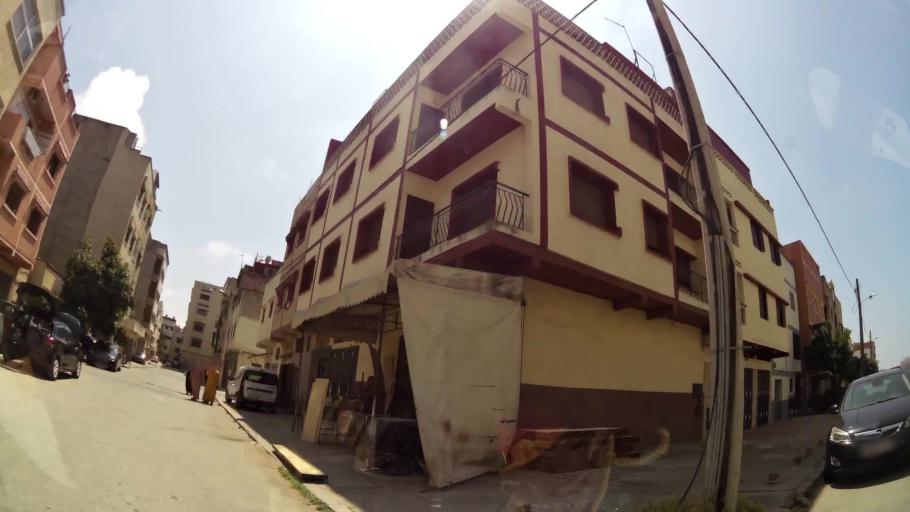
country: MA
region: Rabat-Sale-Zemmour-Zaer
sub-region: Skhirate-Temara
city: Temara
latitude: 33.9725
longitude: -6.8861
